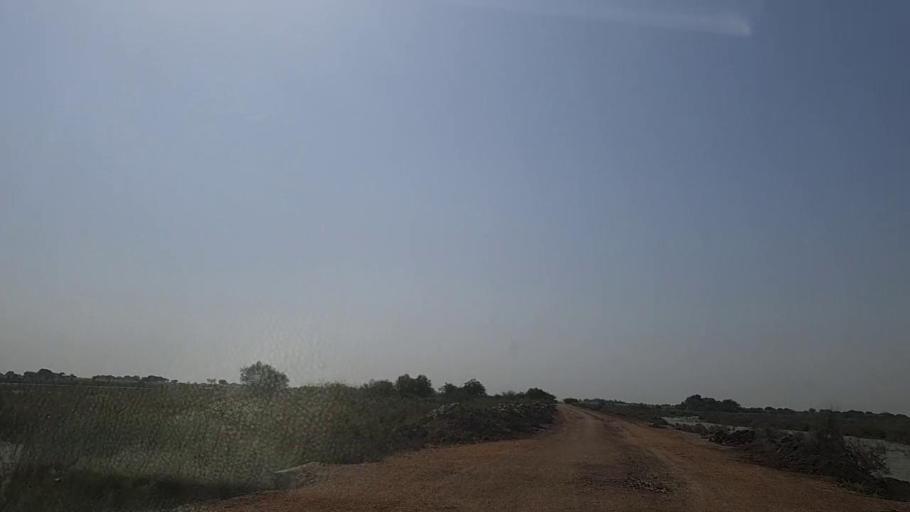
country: PK
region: Sindh
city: Daro Mehar
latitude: 24.7028
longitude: 68.1284
